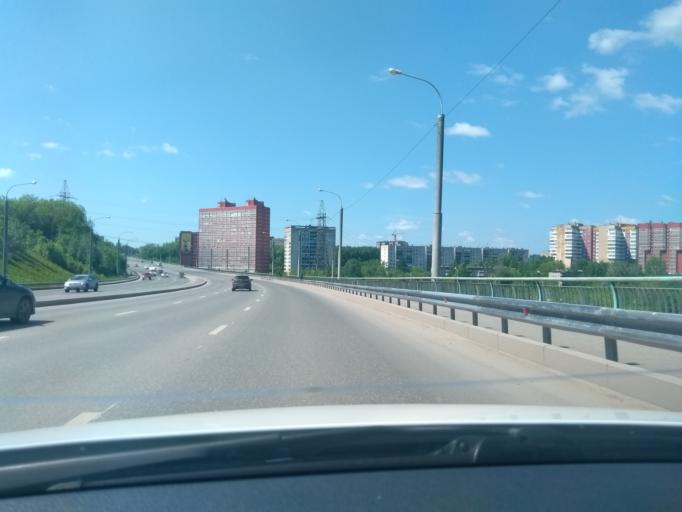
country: RU
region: Perm
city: Perm
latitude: 57.9862
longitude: 56.2378
